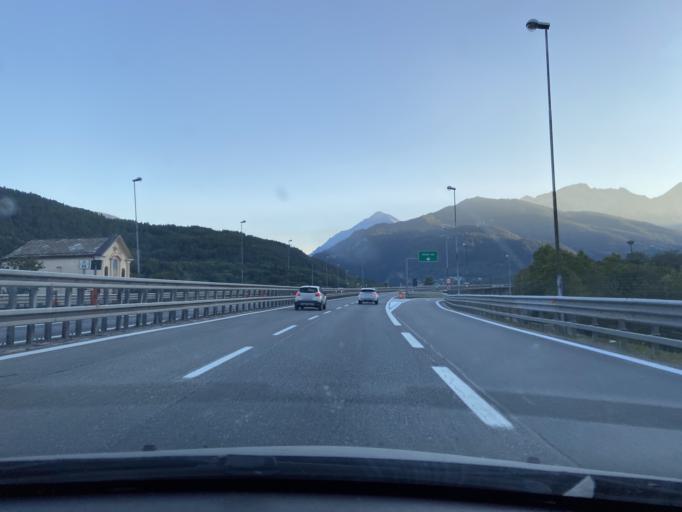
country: IT
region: Piedmont
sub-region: Provincia di Torino
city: Oulx
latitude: 45.0475
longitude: 6.8520
